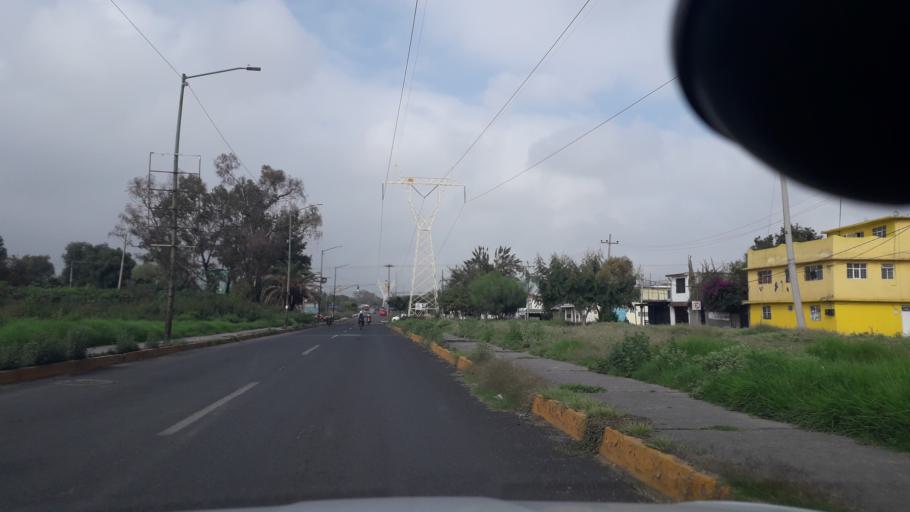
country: MX
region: Mexico
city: Coacalco
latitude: 19.6446
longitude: -99.0892
